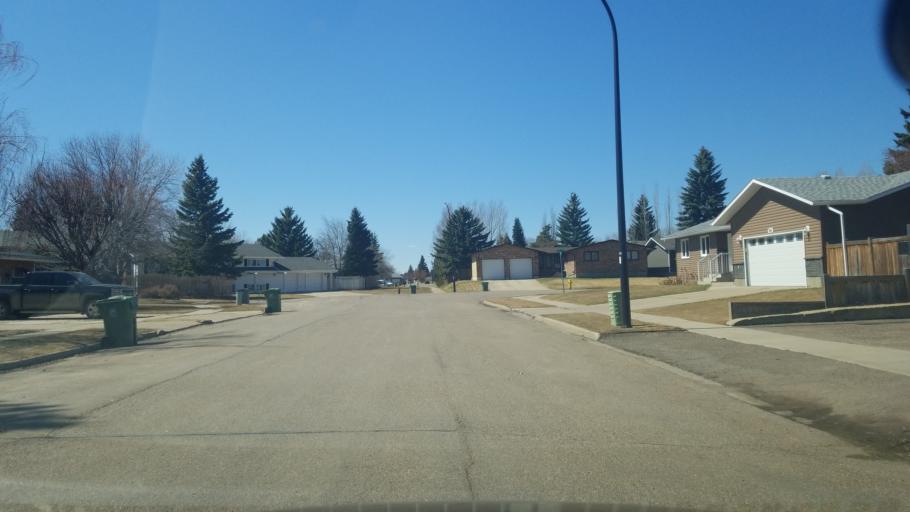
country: CA
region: Saskatchewan
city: Lloydminster
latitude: 53.2639
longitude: -110.0118
